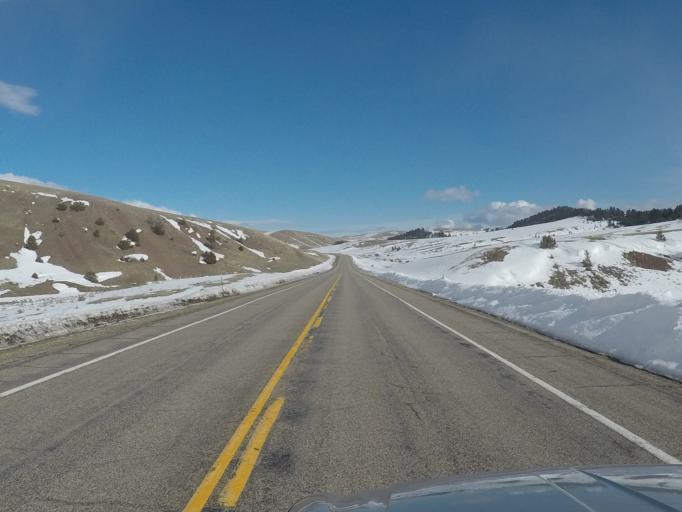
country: US
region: Montana
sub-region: Meagher County
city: White Sulphur Springs
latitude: 46.6217
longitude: -110.7002
